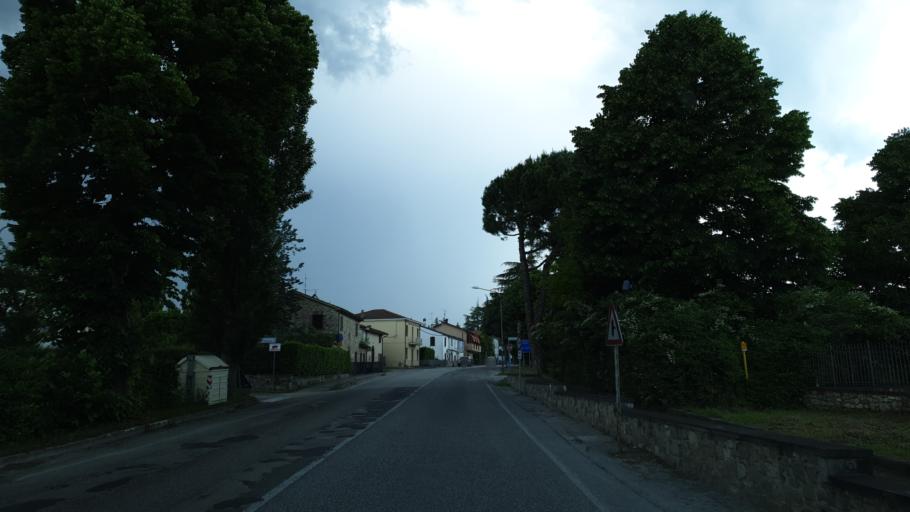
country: IT
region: Emilia-Romagna
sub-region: Provincia di Rimini
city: Secchiano
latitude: 43.9281
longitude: 12.3225
